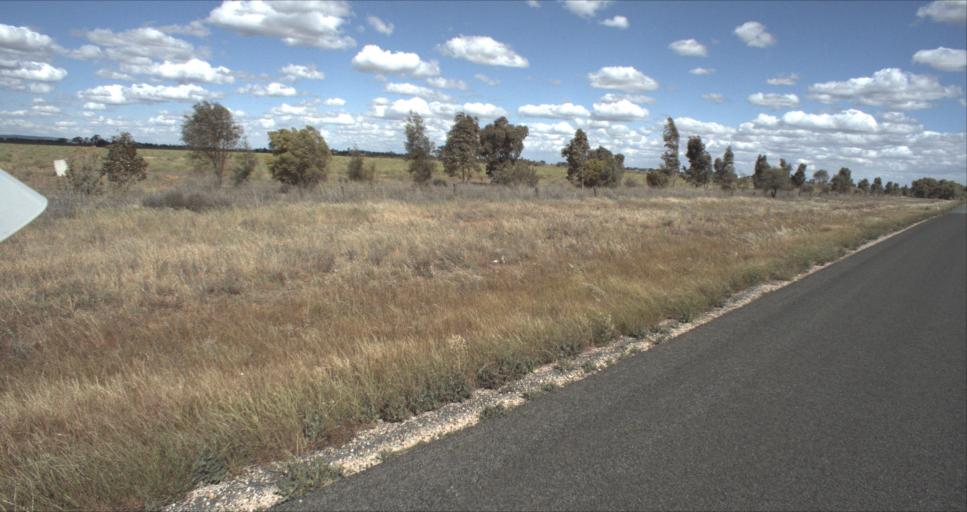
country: AU
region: New South Wales
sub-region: Leeton
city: Leeton
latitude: -34.4382
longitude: 146.2569
